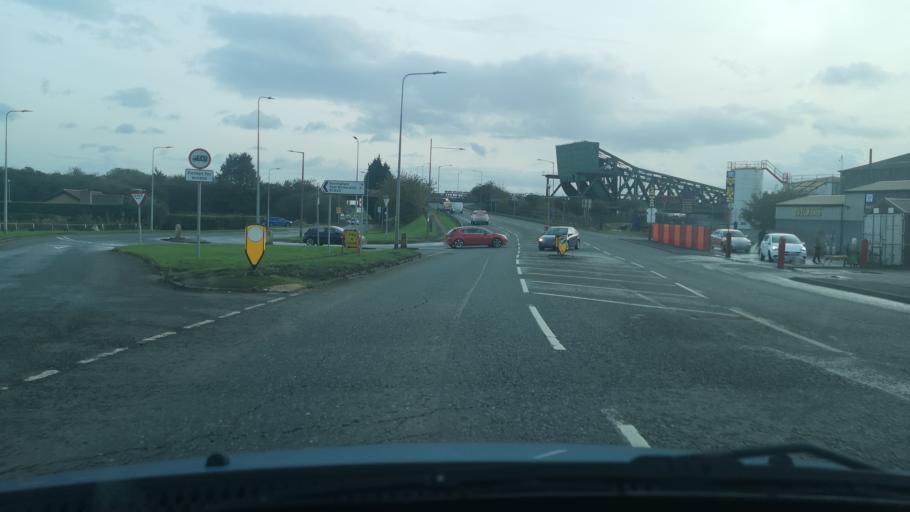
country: GB
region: England
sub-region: North Lincolnshire
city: Gunness
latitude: 53.5876
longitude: -0.7287
